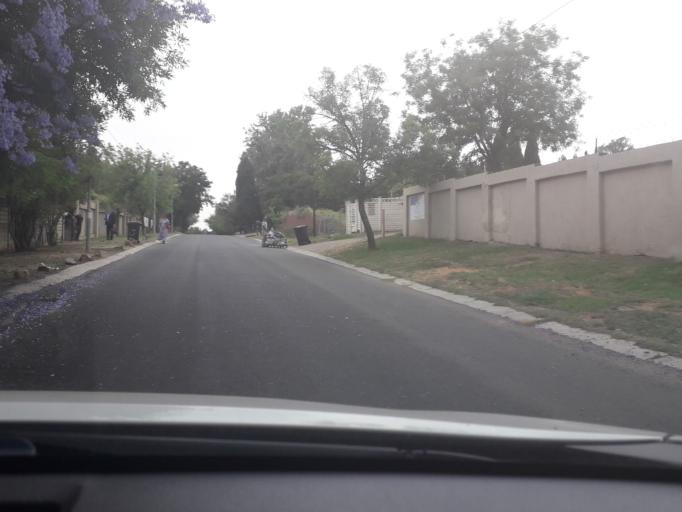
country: ZA
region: Gauteng
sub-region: City of Johannesburg Metropolitan Municipality
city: Johannesburg
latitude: -26.0907
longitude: 27.9933
